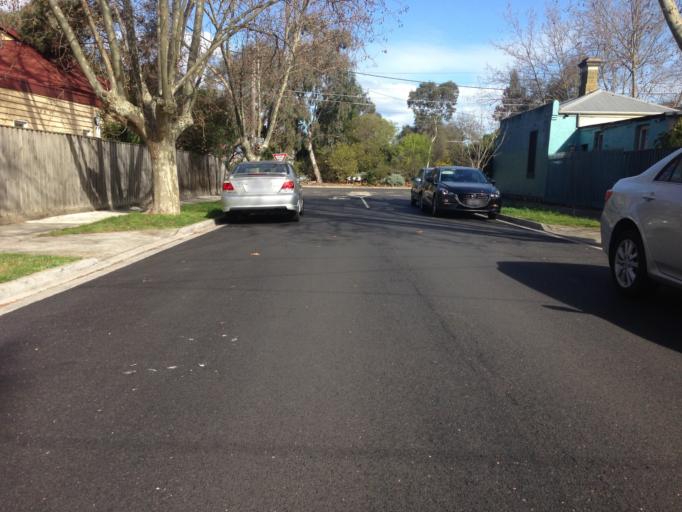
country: AU
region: Victoria
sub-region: Darebin
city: Fairfield
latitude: -37.7786
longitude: 145.0115
